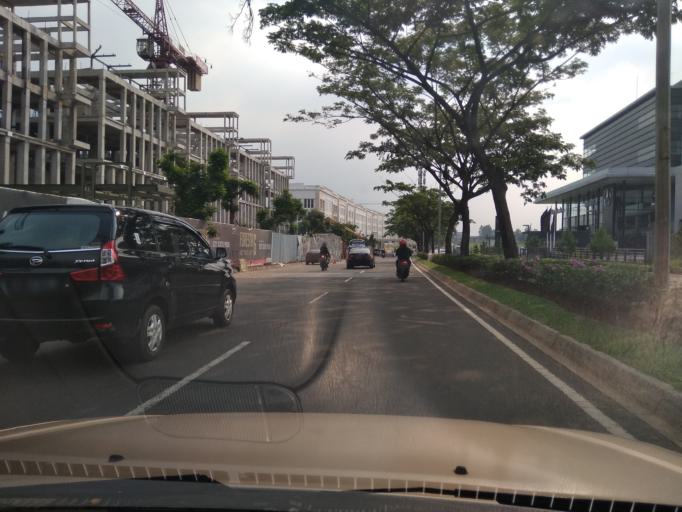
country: ID
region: West Java
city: Serpong
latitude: -6.2888
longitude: 106.6464
